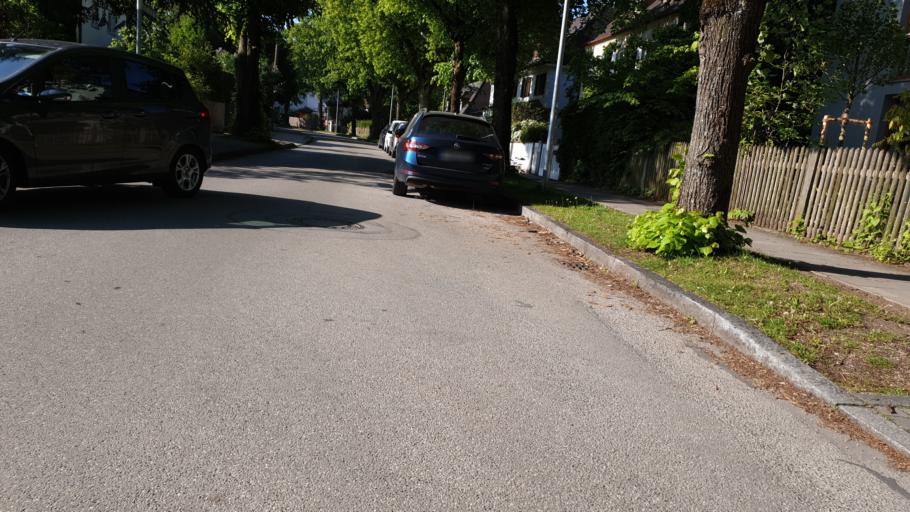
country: DE
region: Bavaria
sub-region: Upper Bavaria
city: Pasing
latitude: 48.1617
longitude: 11.4623
